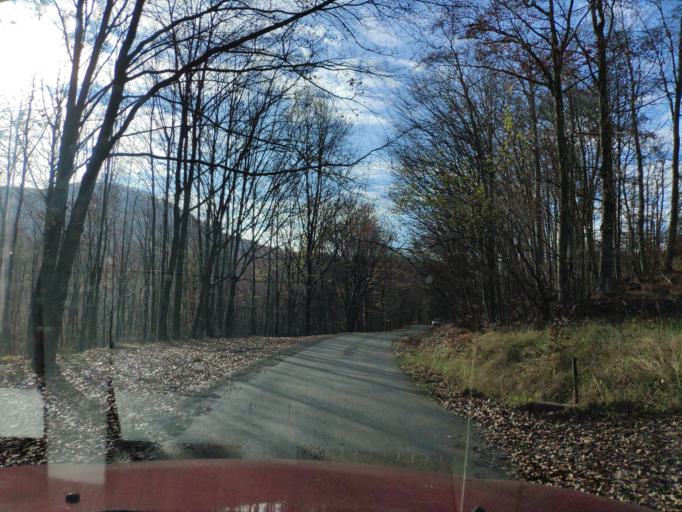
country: HU
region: Borsod-Abauj-Zemplen
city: Gonc
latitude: 48.5997
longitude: 21.4499
